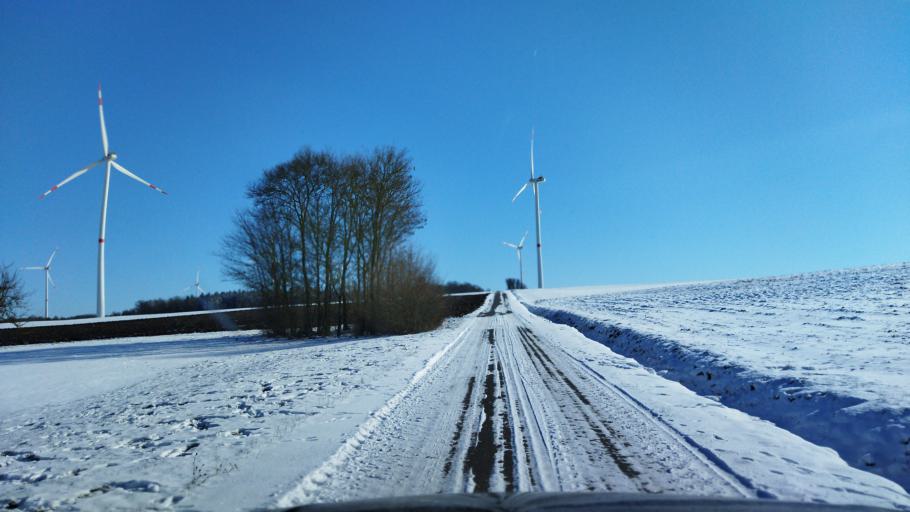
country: DE
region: Baden-Wuerttemberg
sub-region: Regierungsbezirk Stuttgart
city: Ilshofen
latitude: 49.1921
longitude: 9.9407
